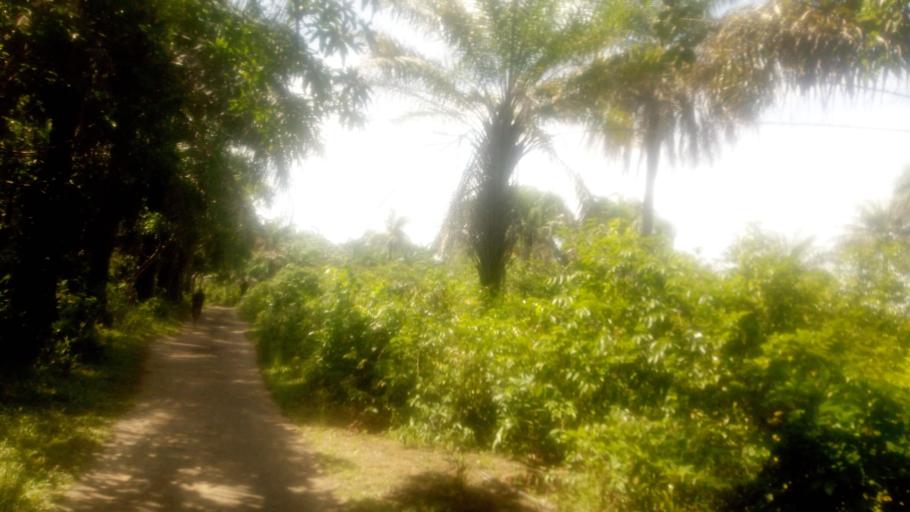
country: SL
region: Northern Province
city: Magburaka
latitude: 8.6602
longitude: -12.0692
